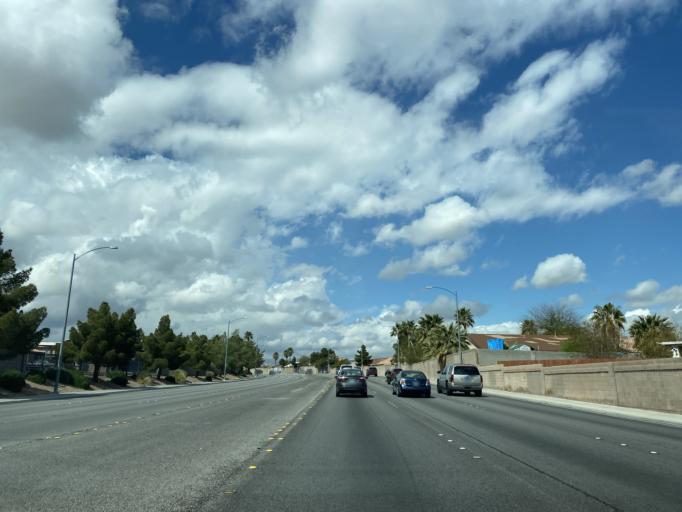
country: US
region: Nevada
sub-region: Clark County
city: Las Vegas
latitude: 36.1968
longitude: -115.1738
